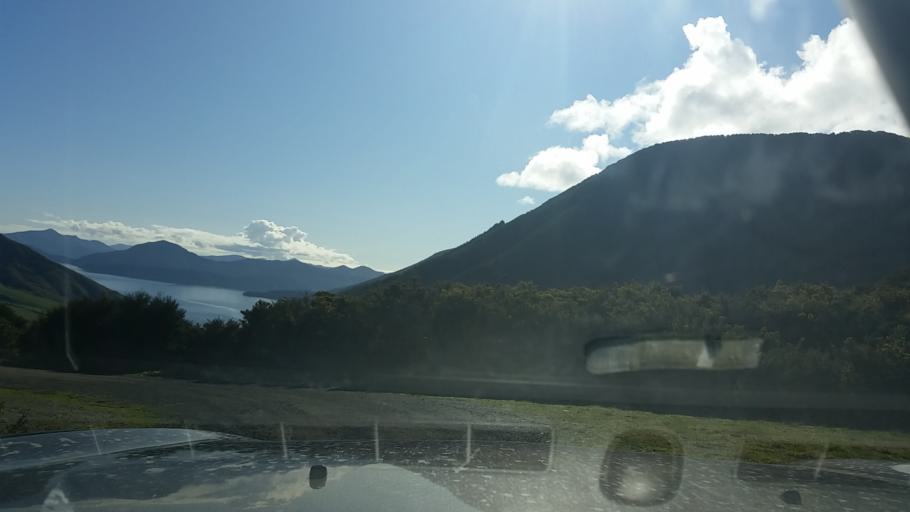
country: NZ
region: Marlborough
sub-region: Marlborough District
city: Picton
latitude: -41.1361
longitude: 174.0578
